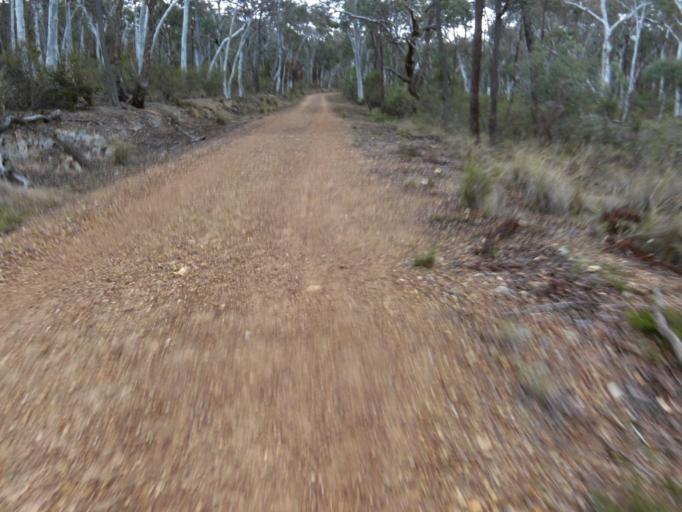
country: AU
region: Australian Capital Territory
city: Acton
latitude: -35.2655
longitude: 149.0941
